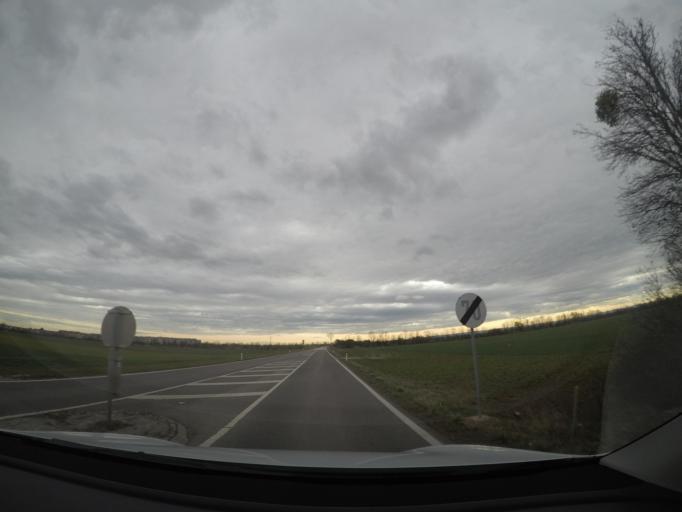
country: AT
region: Lower Austria
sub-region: Politischer Bezirk Modling
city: Vosendorf
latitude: 48.1060
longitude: 16.3429
